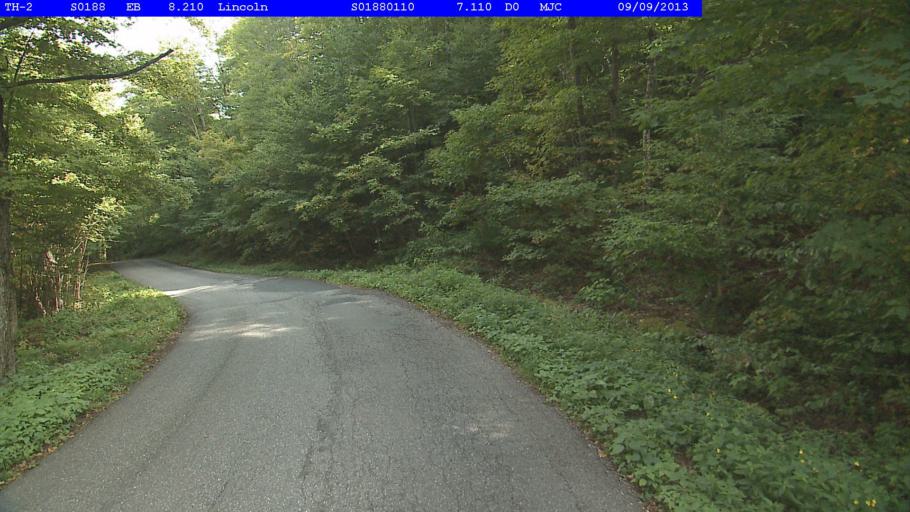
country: US
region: Vermont
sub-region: Addison County
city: Bristol
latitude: 44.0946
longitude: -72.9253
